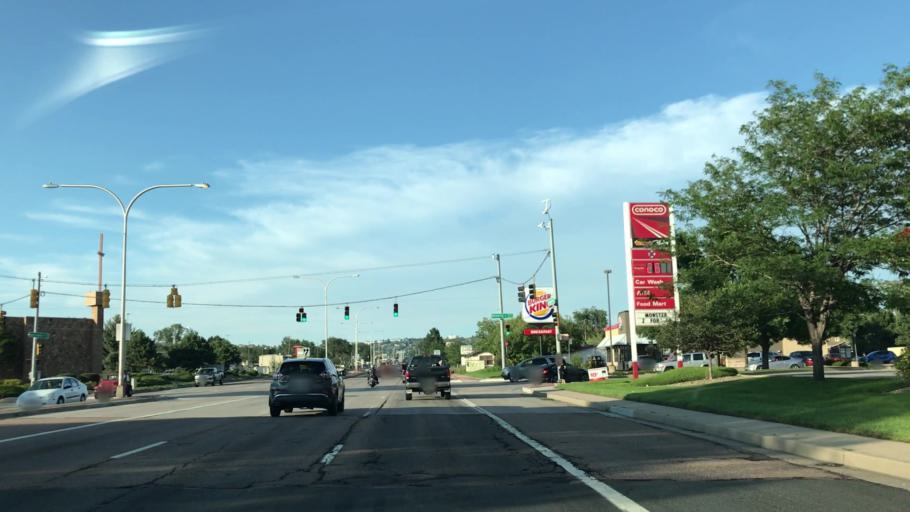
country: US
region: Colorado
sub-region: El Paso County
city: Cimarron Hills
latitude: 38.8924
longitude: -104.7531
